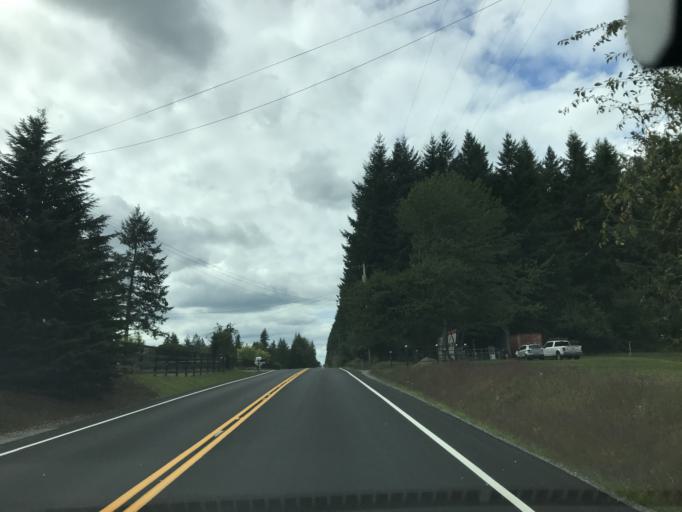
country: US
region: Washington
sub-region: King County
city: Black Diamond
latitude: 47.2868
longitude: -122.0050
